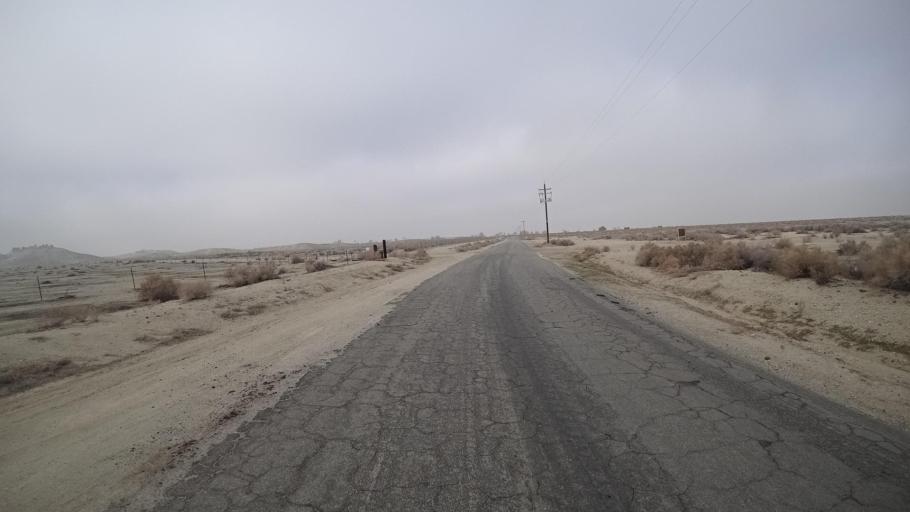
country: US
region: California
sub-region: Kern County
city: Maricopa
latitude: 35.0469
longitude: -119.3912
